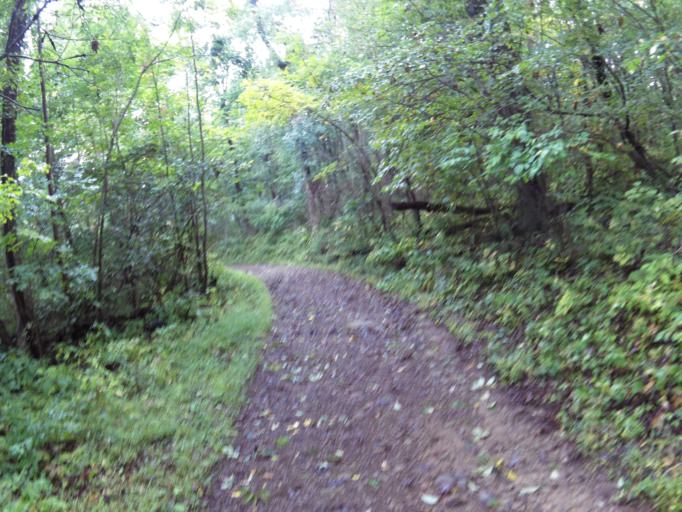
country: US
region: Virginia
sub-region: Rappahannock County
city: Washington
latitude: 38.7697
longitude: -78.2954
